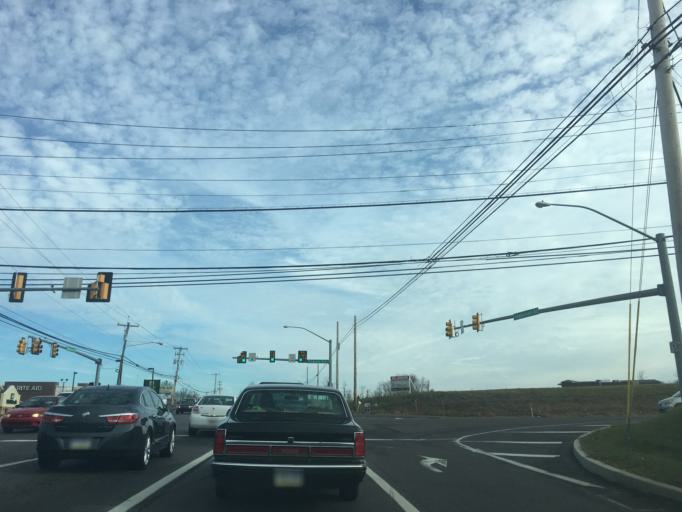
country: US
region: Pennsylvania
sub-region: Dauphin County
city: Progress
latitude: 40.3296
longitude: -76.8577
